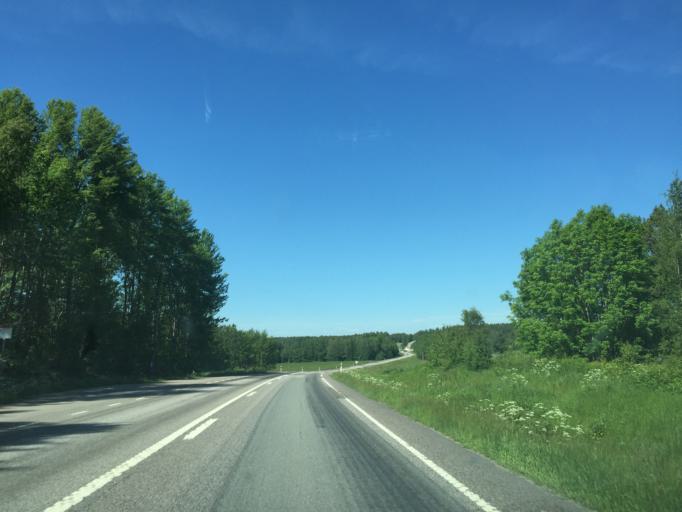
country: SE
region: OEstergoetland
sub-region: Motala Kommun
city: Motala
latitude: 58.6360
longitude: 14.9590
